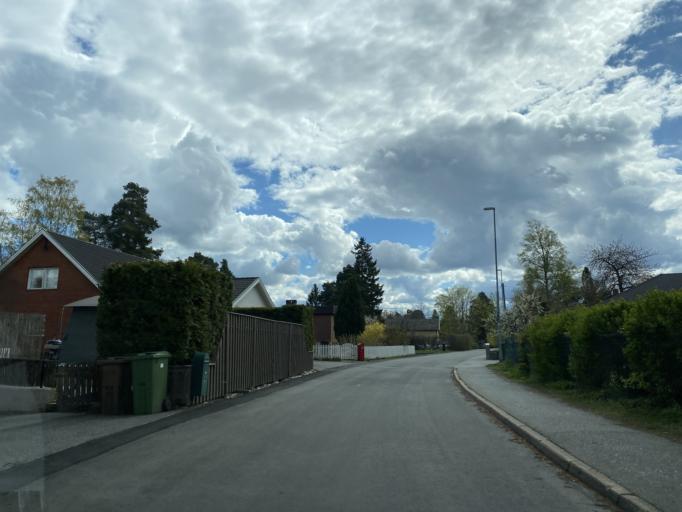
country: SE
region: Stockholm
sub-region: Sollentuna Kommun
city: Sollentuna
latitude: 59.4258
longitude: 17.9373
